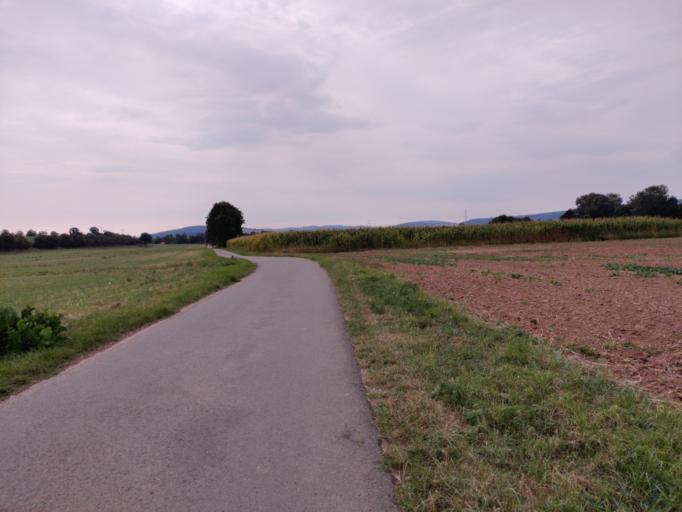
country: DE
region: Lower Saxony
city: Hehlen
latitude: 52.0389
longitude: 9.4173
